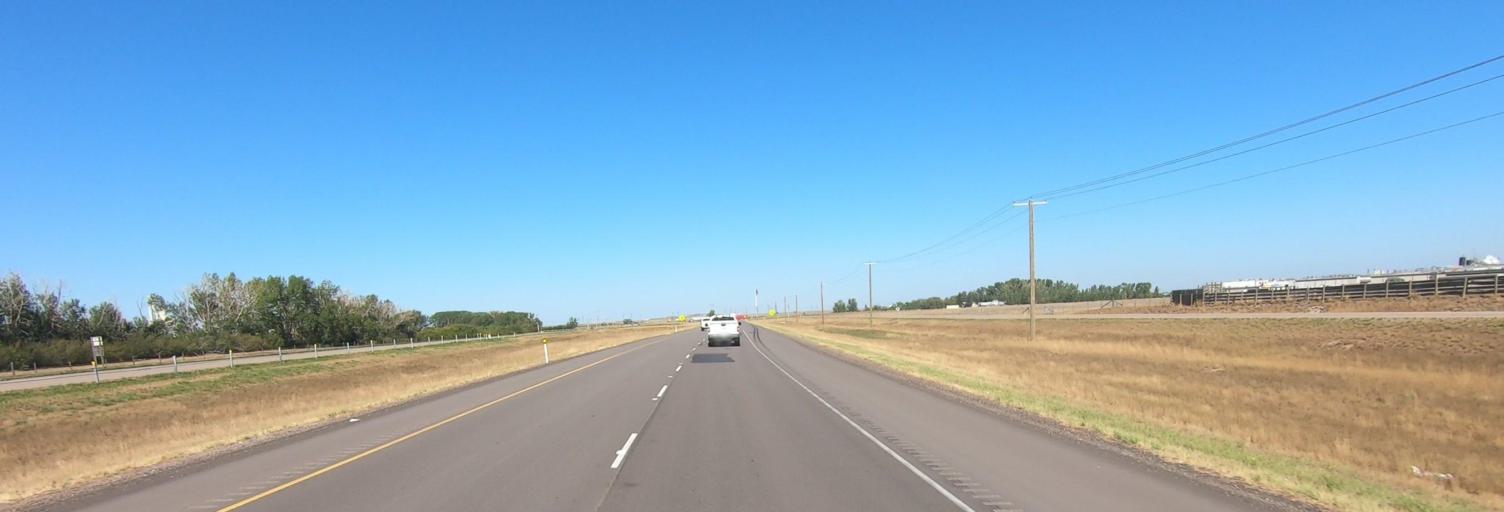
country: CA
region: Alberta
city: Brooks
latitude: 50.6107
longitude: -111.9340
